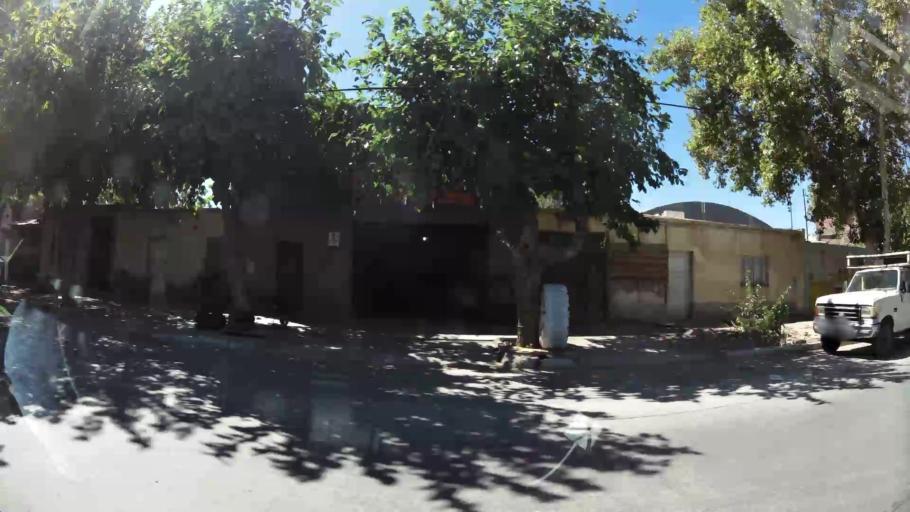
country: AR
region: San Juan
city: Villa Krause
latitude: -31.5585
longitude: -68.5238
